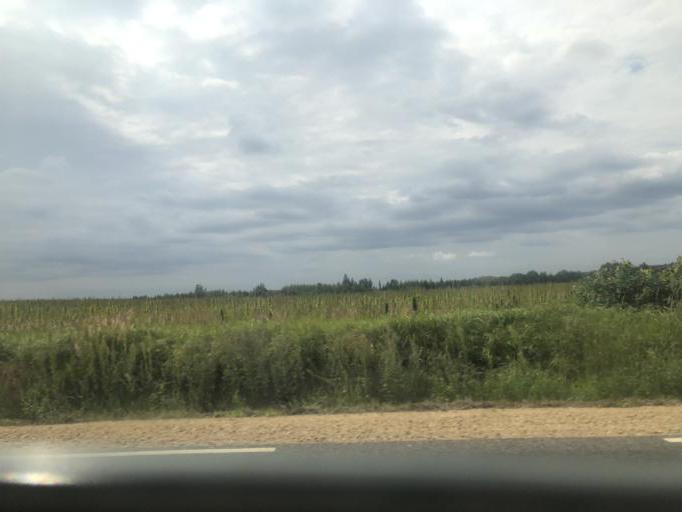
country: LV
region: Baldone
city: Baldone
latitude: 56.7324
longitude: 24.3596
